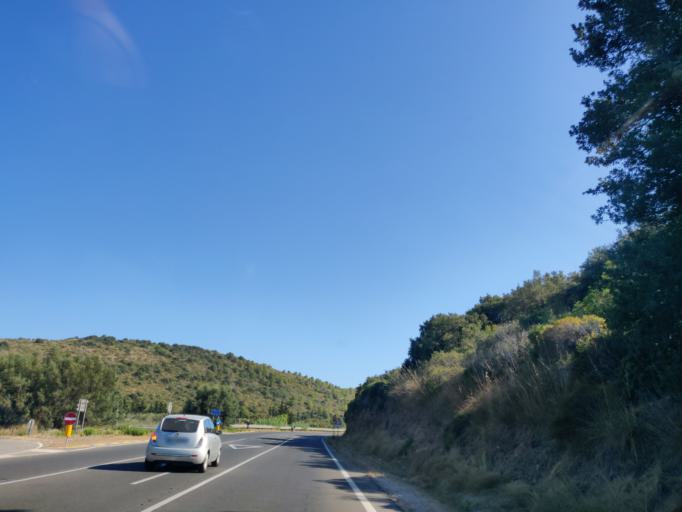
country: IT
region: Tuscany
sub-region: Provincia di Grosseto
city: Porto Ercole
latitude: 42.4166
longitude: 11.2042
